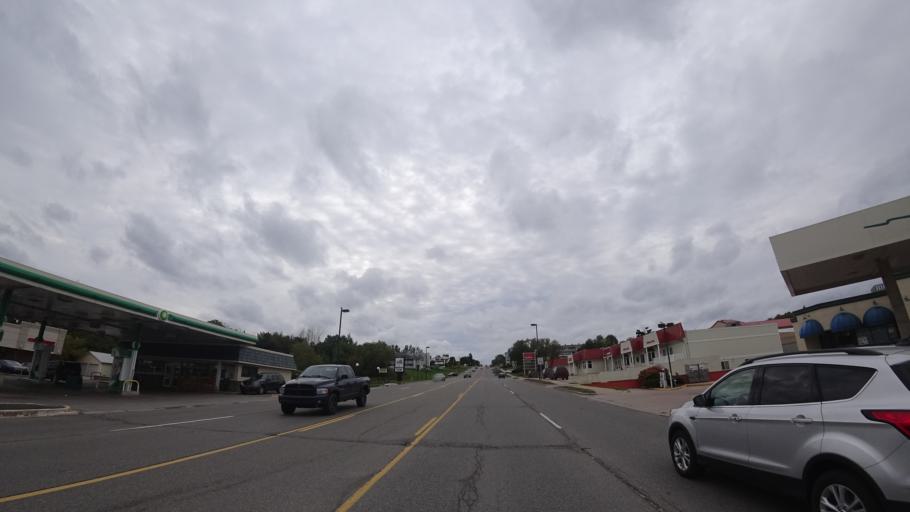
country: US
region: Michigan
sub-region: Emmet County
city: Petoskey
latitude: 45.3691
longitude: -84.9709
